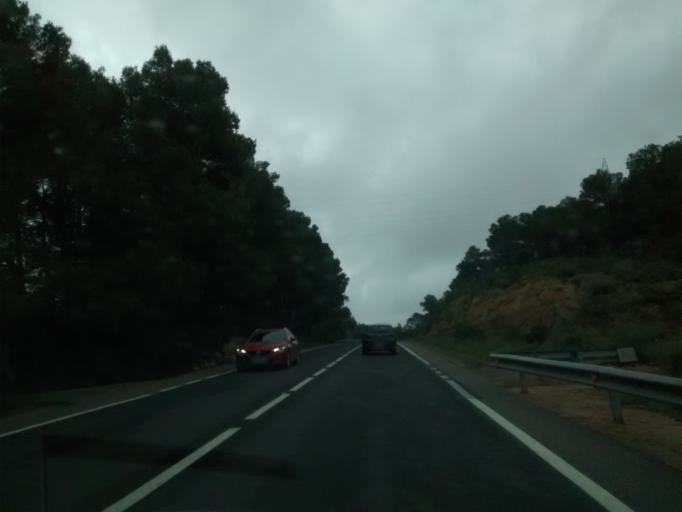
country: ES
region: Catalonia
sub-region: Provincia de Tarragona
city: Bot
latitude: 41.0591
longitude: 0.3566
